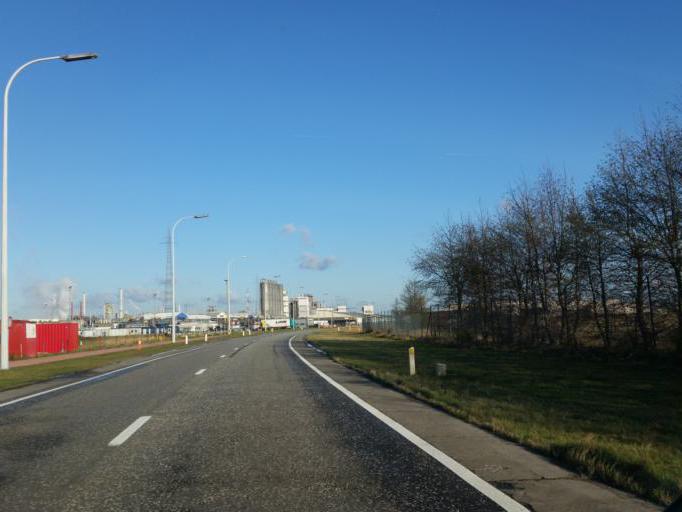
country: BE
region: Flanders
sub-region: Provincie Antwerpen
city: Zwijndrecht
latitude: 51.2346
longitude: 4.3277
